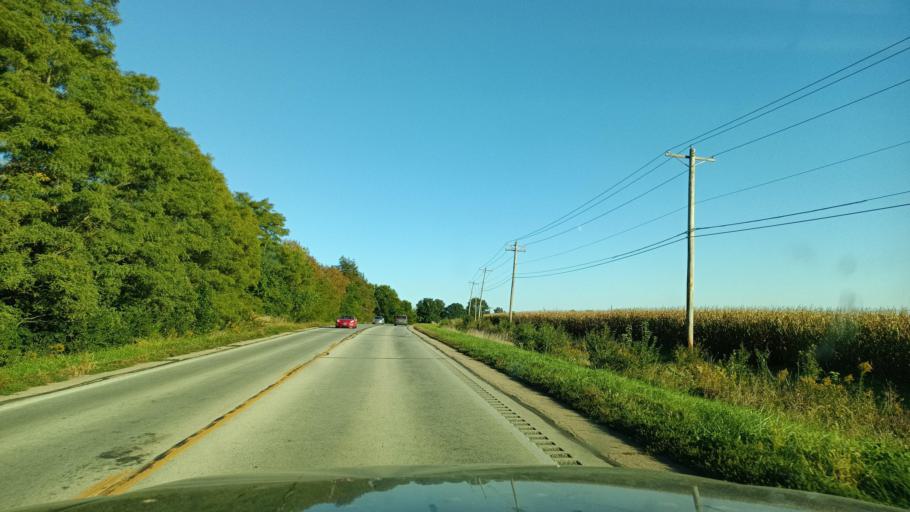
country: US
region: Illinois
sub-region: Champaign County
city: Lake of the Woods
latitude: 40.1633
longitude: -88.3200
